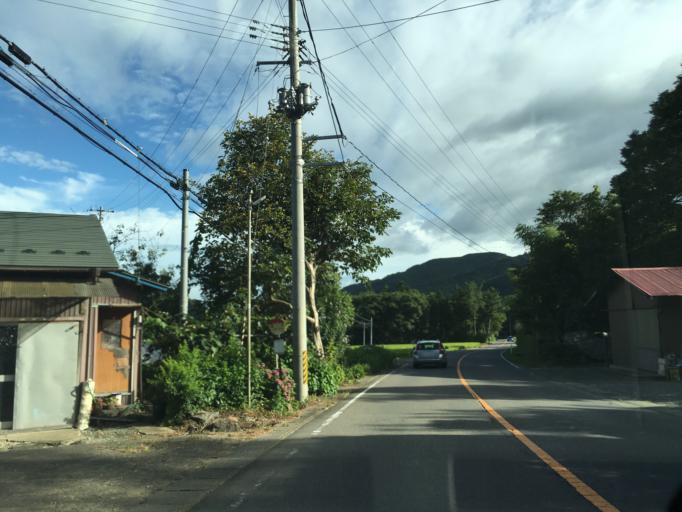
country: JP
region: Fukushima
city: Motomiya
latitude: 37.5170
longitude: 140.2703
